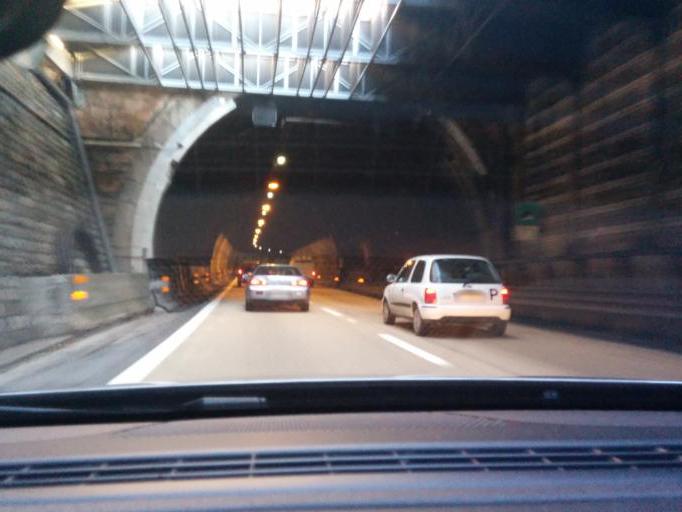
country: IT
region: Liguria
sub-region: Provincia di Genova
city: Genoa
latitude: 44.4292
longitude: 8.8977
